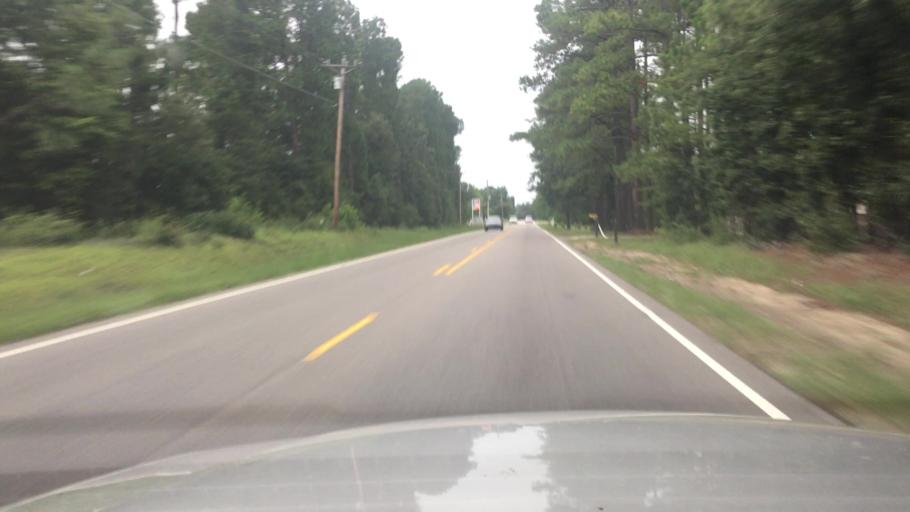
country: US
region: North Carolina
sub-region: Hoke County
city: Rockfish
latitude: 34.9765
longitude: -79.0575
